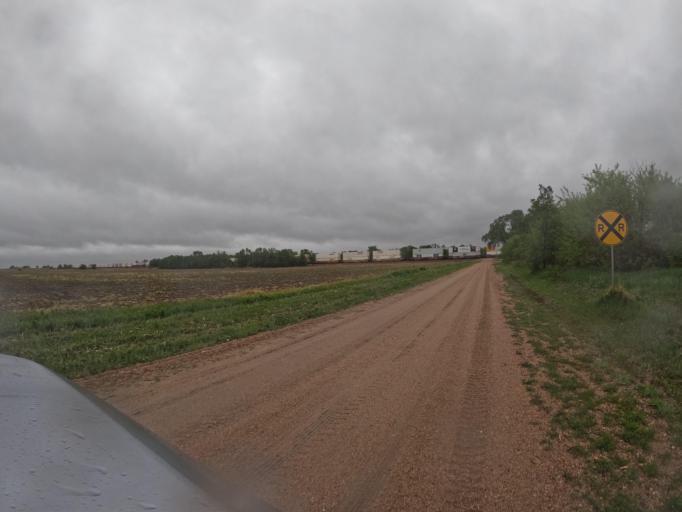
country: US
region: Nebraska
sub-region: Clay County
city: Harvard
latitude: 40.6154
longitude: -98.1027
